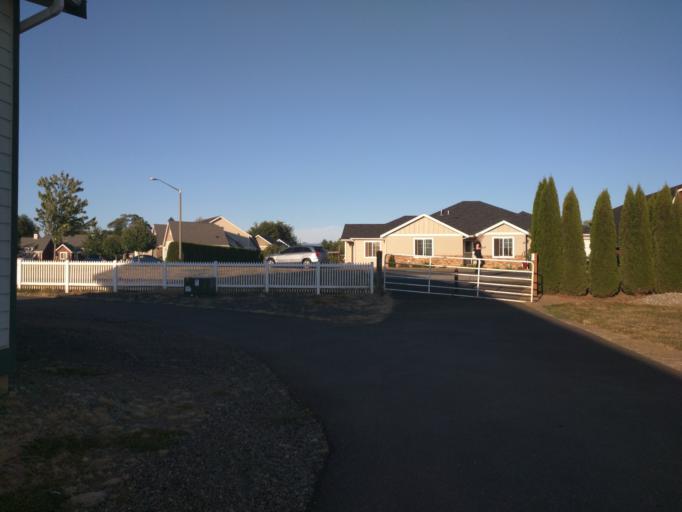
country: US
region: Washington
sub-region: Whatcom County
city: Lynden
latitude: 48.9595
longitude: -122.4358
